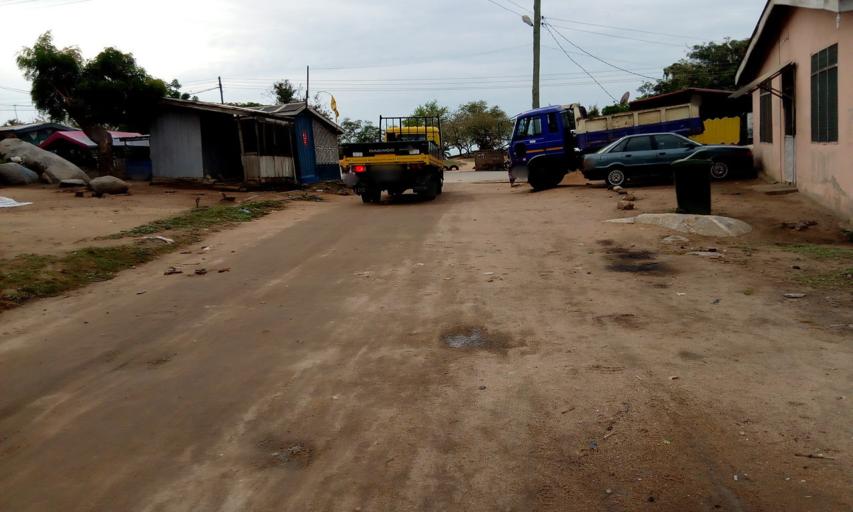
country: GH
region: Central
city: Winneba
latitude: 5.3531
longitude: -0.6179
